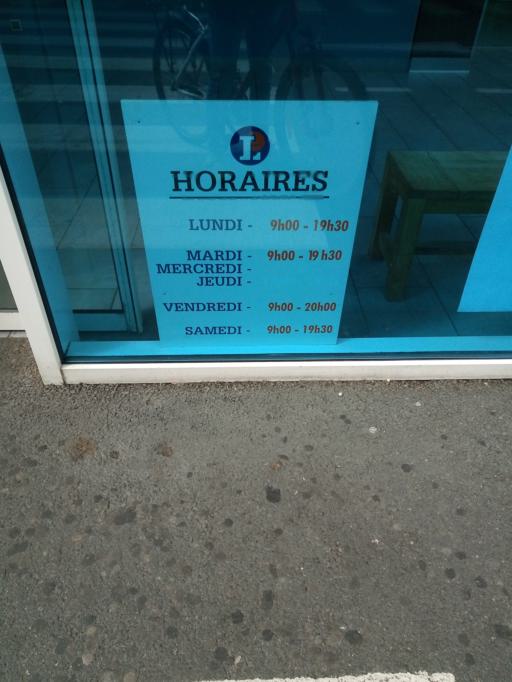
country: FR
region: Brittany
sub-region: Departement du Morbihan
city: Gourin
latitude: 48.1426
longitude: -3.6191
